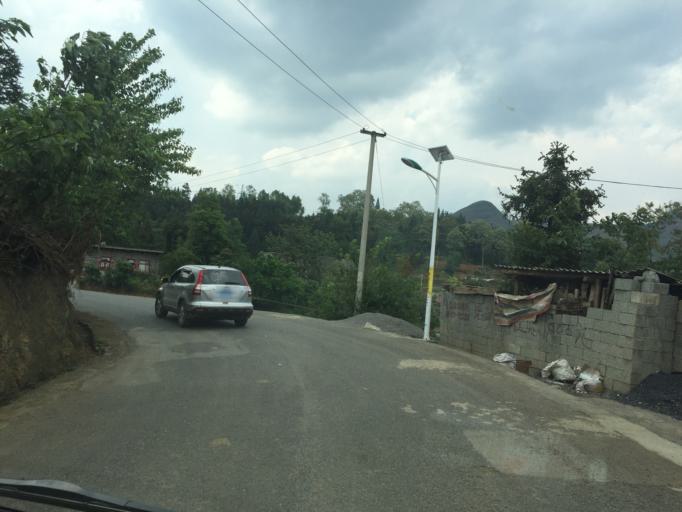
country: CN
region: Guangxi Zhuangzu Zizhiqu
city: Xinzhou
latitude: 25.6604
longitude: 105.2406
